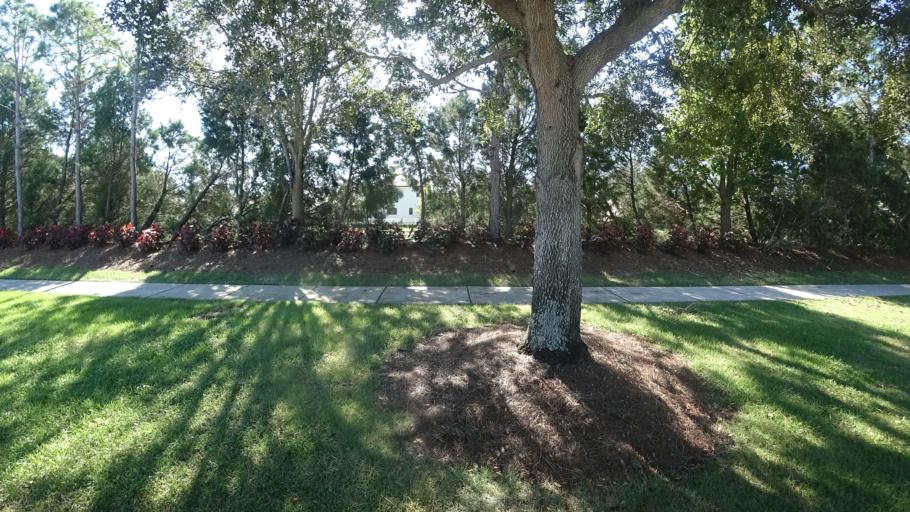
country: US
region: Florida
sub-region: Sarasota County
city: The Meadows
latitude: 27.4237
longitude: -82.3919
